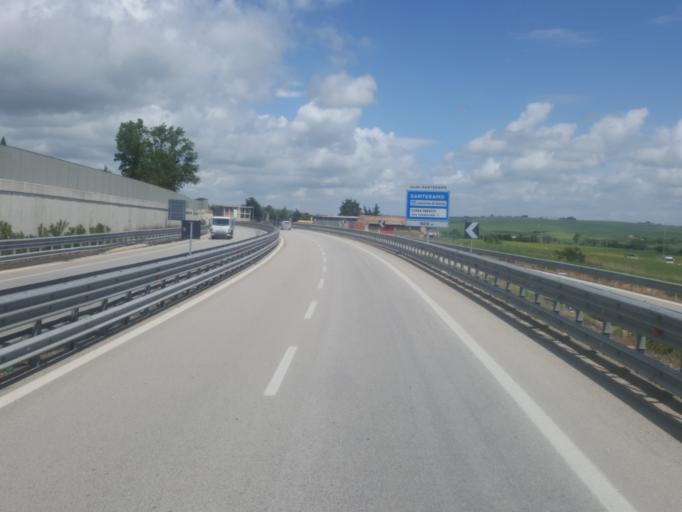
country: IT
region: Basilicate
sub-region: Provincia di Matera
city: Matera
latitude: 40.6929
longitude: 16.5916
